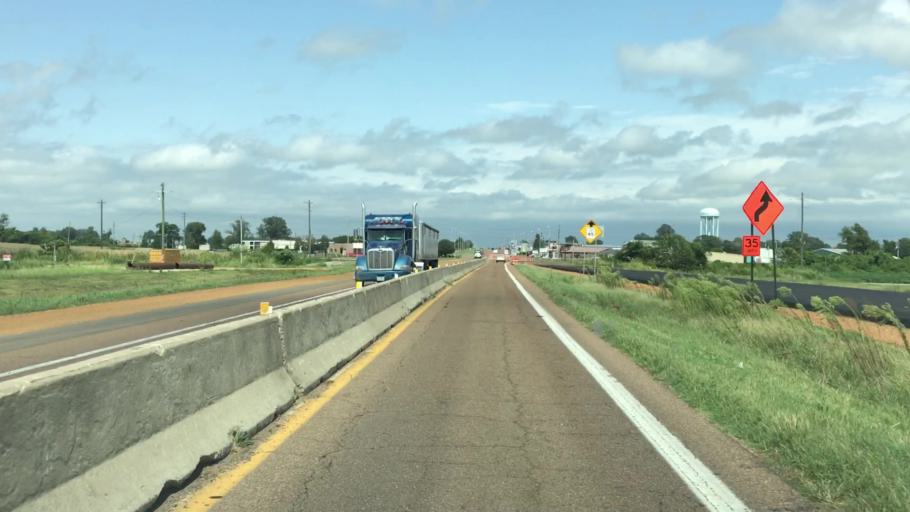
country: US
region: Tennessee
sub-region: Obion County
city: Union City
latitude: 36.3996
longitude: -89.0918
